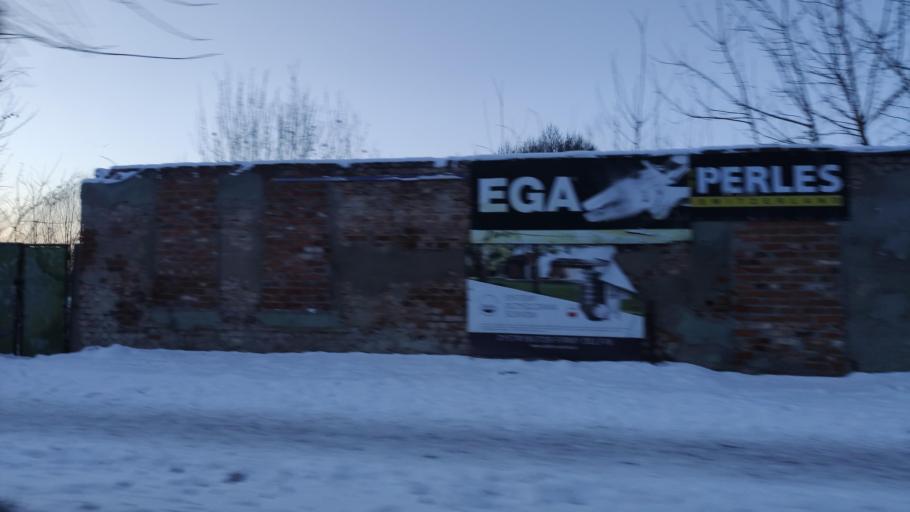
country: PL
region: Kujawsko-Pomorskie
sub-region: Powiat zninski
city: Barcin
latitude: 52.8615
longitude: 17.9466
